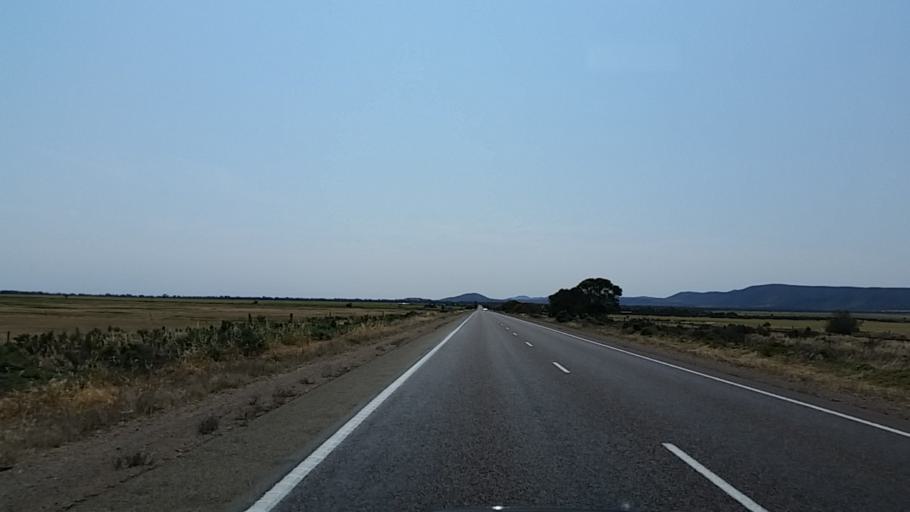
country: AU
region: South Australia
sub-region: Port Pirie City and Dists
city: Port Pirie
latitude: -32.8972
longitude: 137.9823
